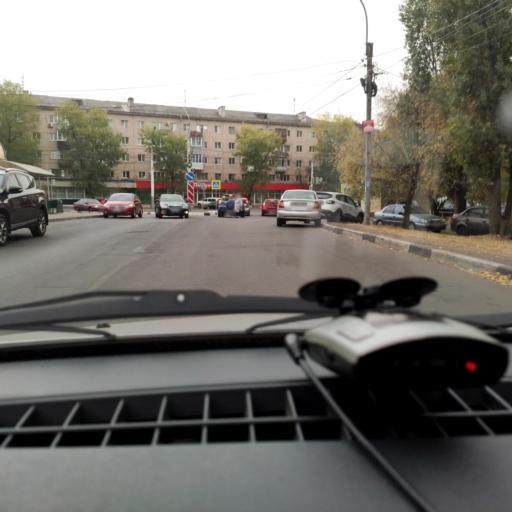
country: RU
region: Voronezj
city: Voronezh
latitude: 51.6559
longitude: 39.2430
